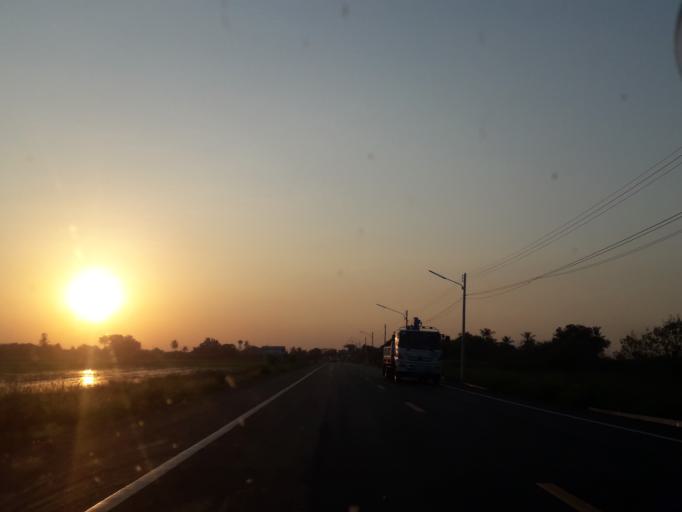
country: TH
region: Pathum Thani
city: Nong Suea
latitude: 14.1317
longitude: 100.7611
